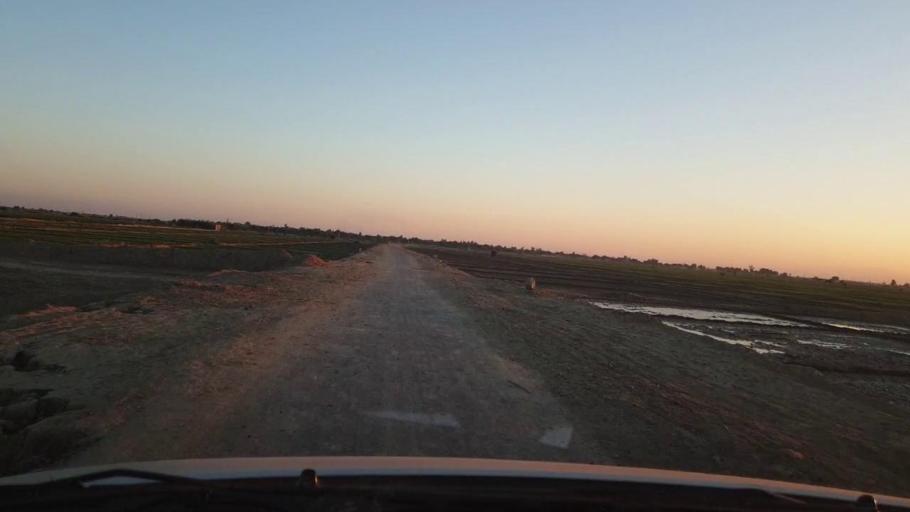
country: PK
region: Sindh
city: Johi
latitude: 26.8398
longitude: 67.4410
